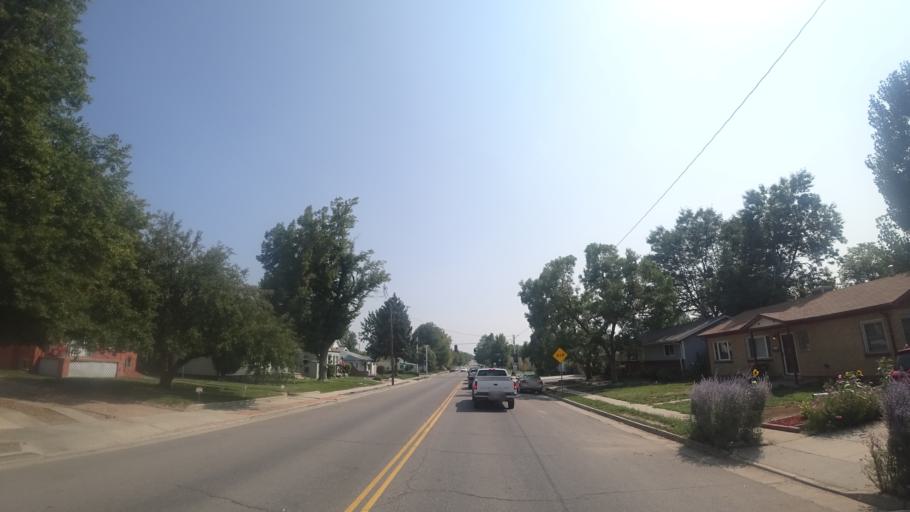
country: US
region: Colorado
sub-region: Arapahoe County
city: Englewood
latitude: 39.6339
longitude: -104.9832
